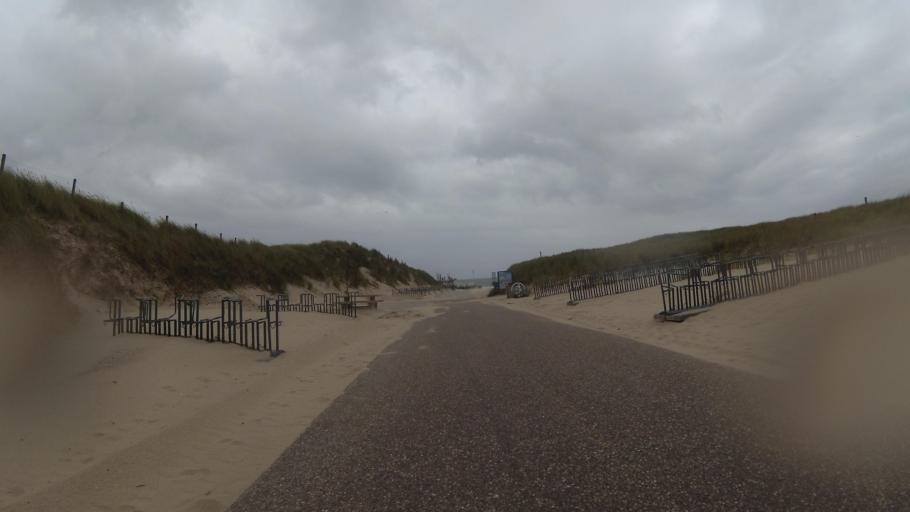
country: NL
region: North Holland
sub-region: Gemeente Den Helder
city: Den Helder
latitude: 52.8646
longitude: 4.7049
